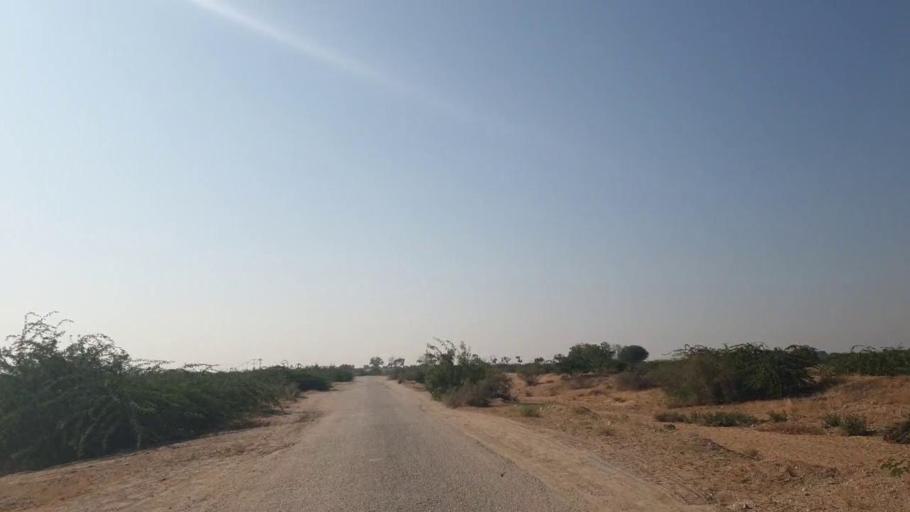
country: PK
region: Sindh
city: Thatta
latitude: 25.1411
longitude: 67.7723
